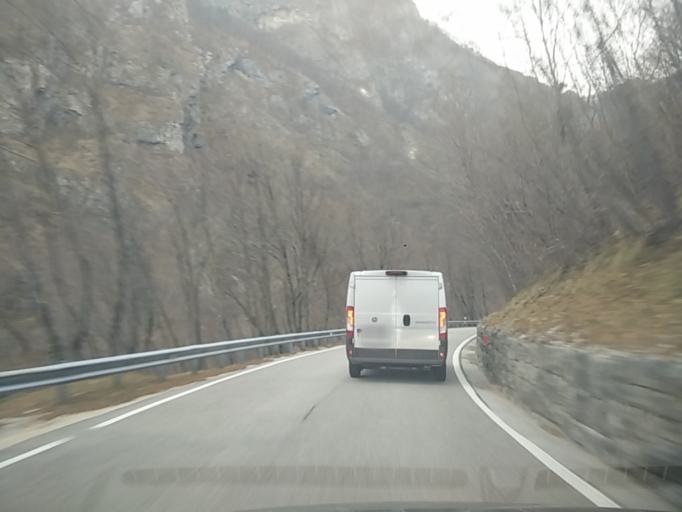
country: IT
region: Veneto
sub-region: Provincia di Treviso
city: Cison di Valmarino
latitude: 45.9964
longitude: 12.1737
